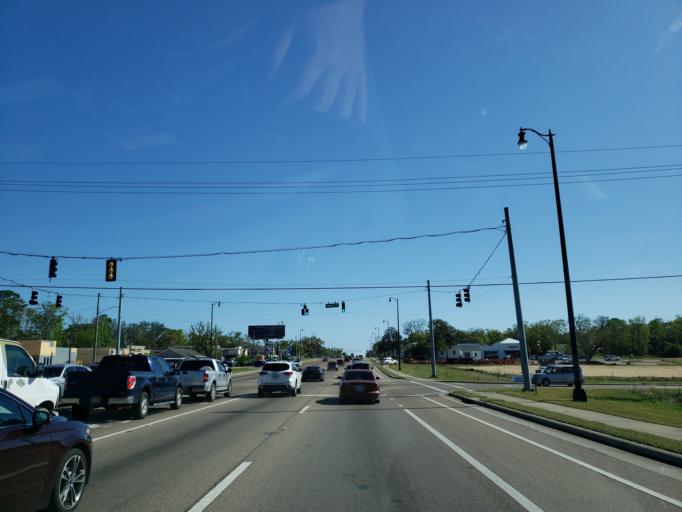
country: US
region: Mississippi
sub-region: Harrison County
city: West Gulfport
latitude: 30.4037
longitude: -89.0269
